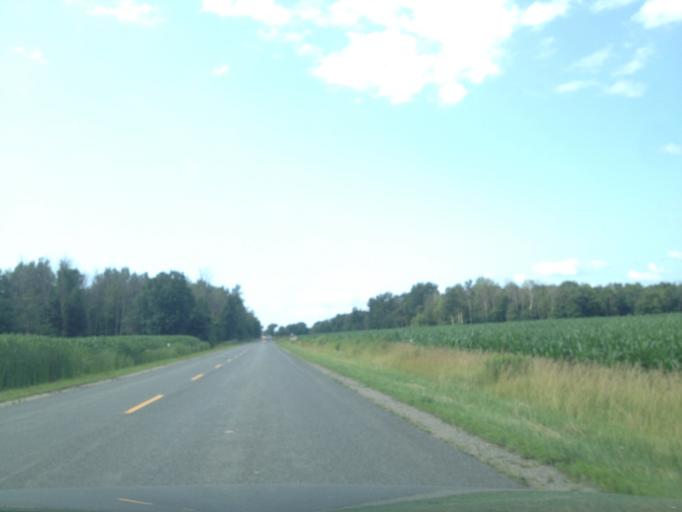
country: CA
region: Ontario
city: Aylmer
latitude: 42.6836
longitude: -80.8598
